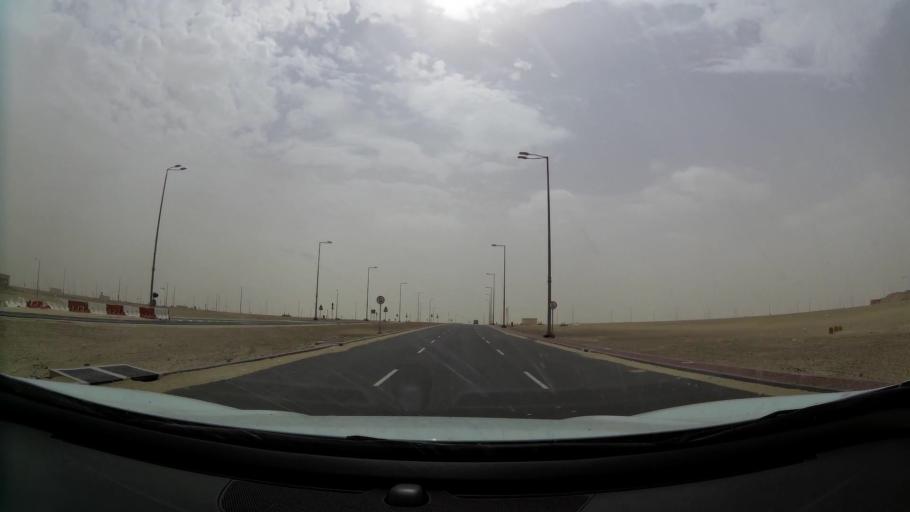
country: AE
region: Abu Dhabi
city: Abu Dhabi
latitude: 24.3530
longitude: 54.7615
